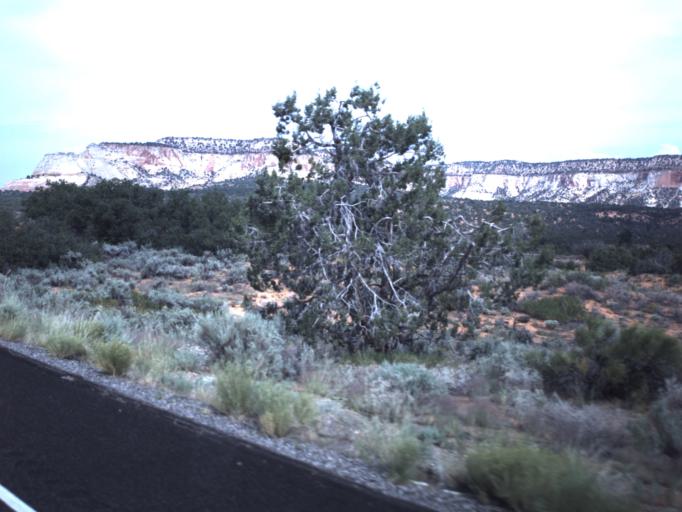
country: US
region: Utah
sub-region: Kane County
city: Kanab
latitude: 37.1682
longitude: -112.6066
